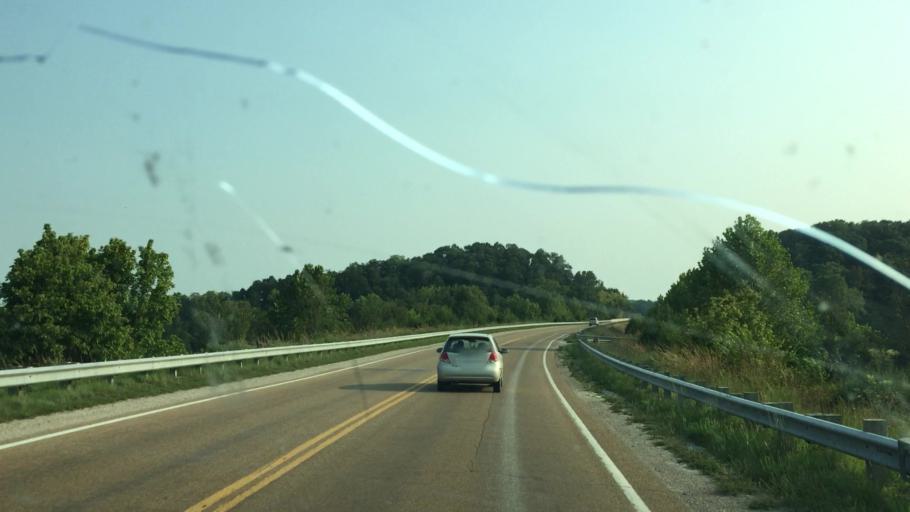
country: US
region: Missouri
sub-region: Pulaski County
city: Richland
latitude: 37.8038
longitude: -92.4051
